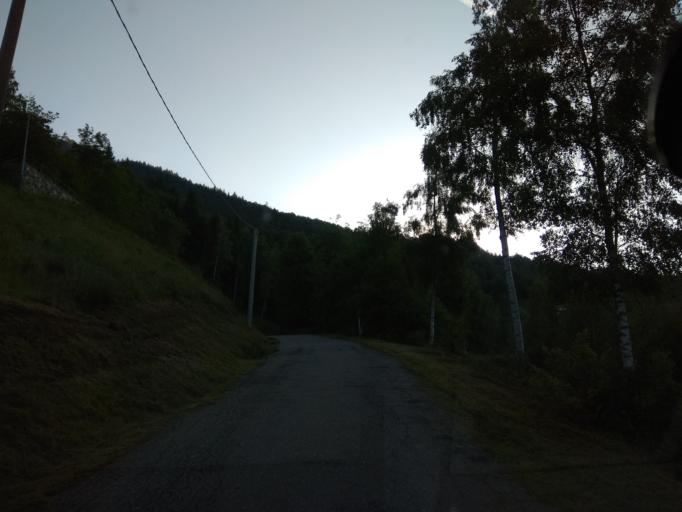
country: IT
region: Piedmont
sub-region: Provincia di Biella
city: Coggiola
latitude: 45.7066
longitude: 8.1718
